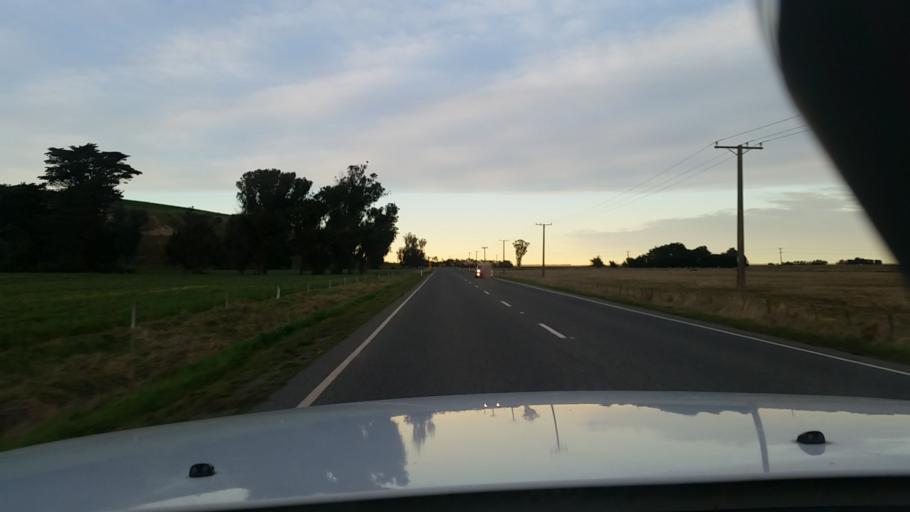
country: NZ
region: Canterbury
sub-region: Selwyn District
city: Lincoln
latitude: -43.7407
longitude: 172.6113
